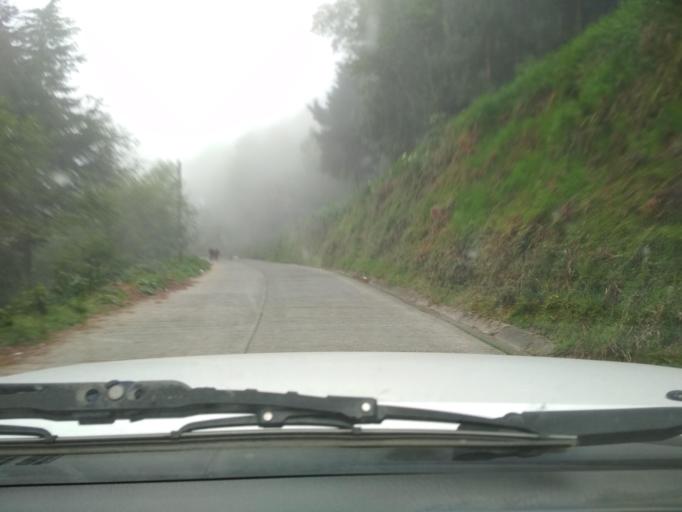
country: MX
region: Veracruz
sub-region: La Perla
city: Chilapa
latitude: 18.9978
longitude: -97.1597
